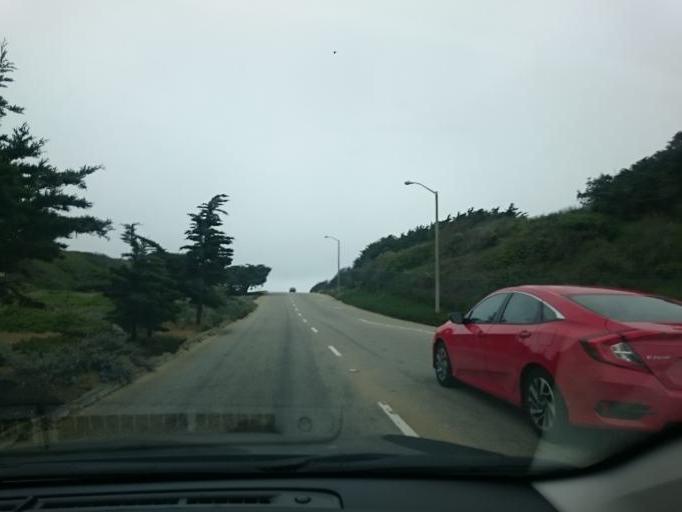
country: US
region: California
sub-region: San Mateo County
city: Broadmoor
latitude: 37.7254
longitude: -122.5033
